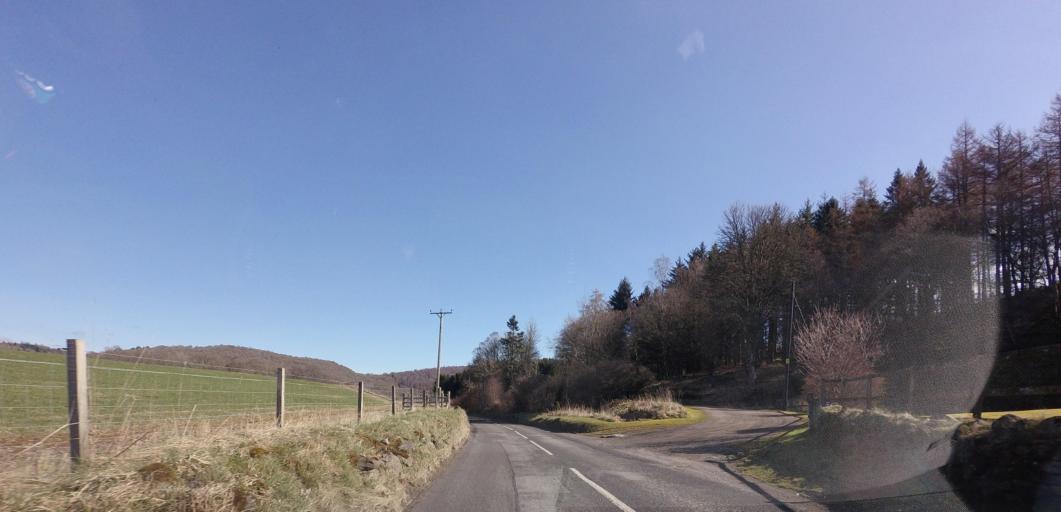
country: GB
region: Scotland
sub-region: Perth and Kinross
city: Bankfoot
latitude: 56.5577
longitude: -3.5904
